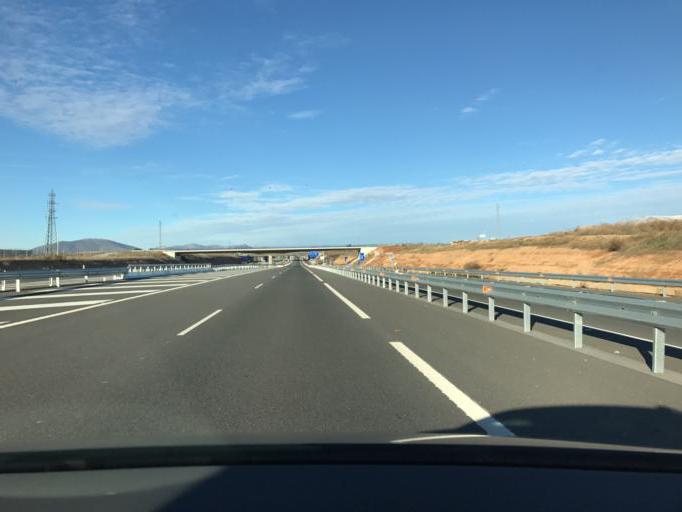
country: ES
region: Andalusia
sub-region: Provincia de Granada
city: Albolote
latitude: 37.2278
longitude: -3.6669
